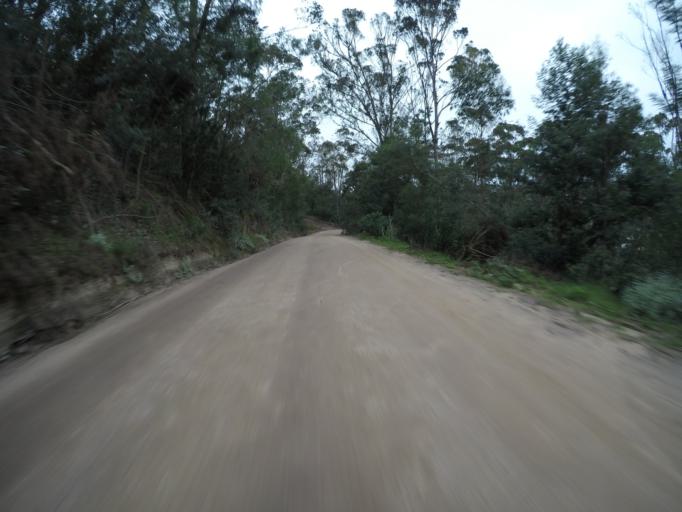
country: ZA
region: Western Cape
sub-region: Eden District Municipality
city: Knysna
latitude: -34.0149
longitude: 22.8126
